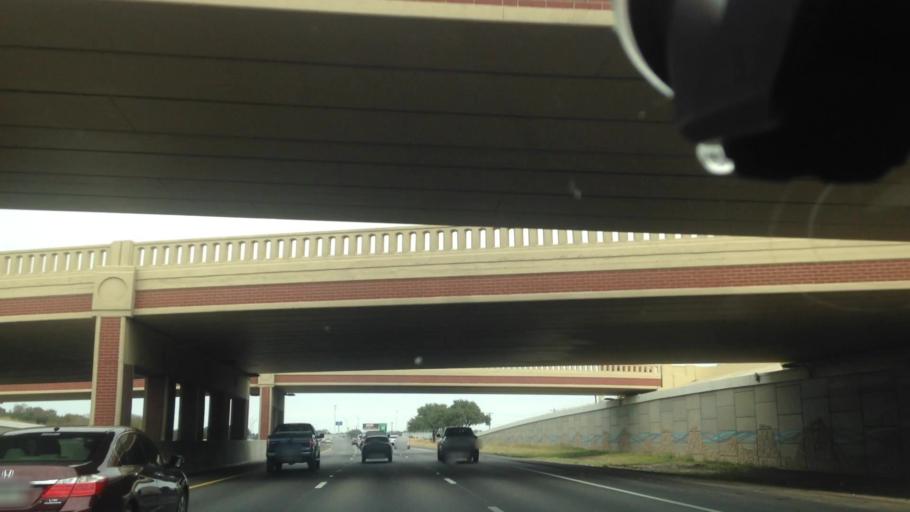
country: US
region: Texas
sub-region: Hays County
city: Kyle
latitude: 29.9467
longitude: -97.8804
